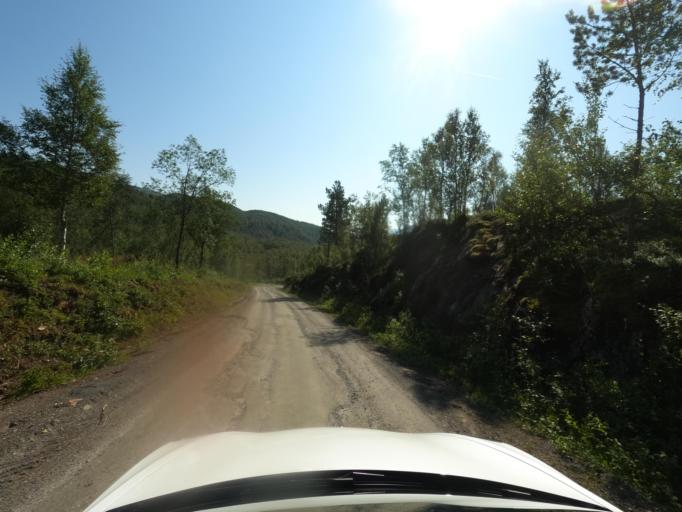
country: NO
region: Nordland
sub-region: Ballangen
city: Ballangen
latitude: 68.2621
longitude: 16.7131
